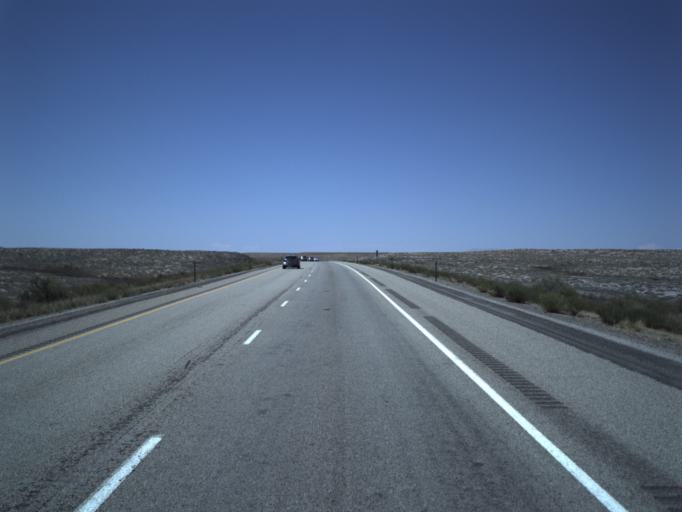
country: US
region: Utah
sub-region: Grand County
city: Moab
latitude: 38.9723
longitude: -109.3623
